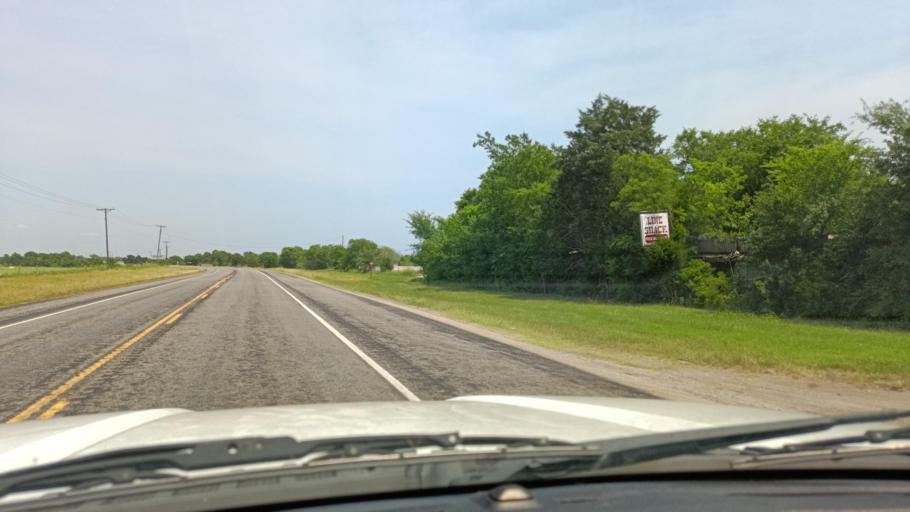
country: US
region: Texas
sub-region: Milam County
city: Cameron
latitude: 30.8498
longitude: -97.0799
